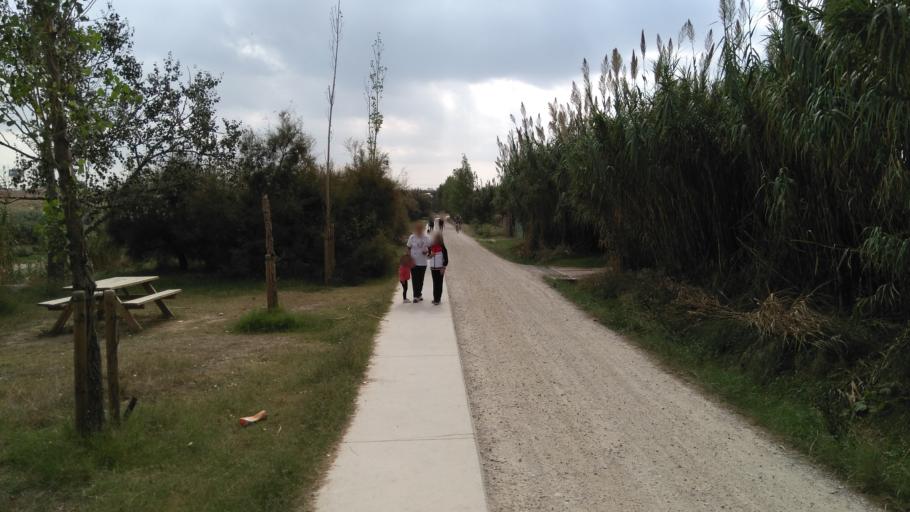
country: ES
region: Catalonia
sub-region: Provincia de Barcelona
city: Sant Vicenc dels Horts
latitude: 41.3948
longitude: 2.0190
